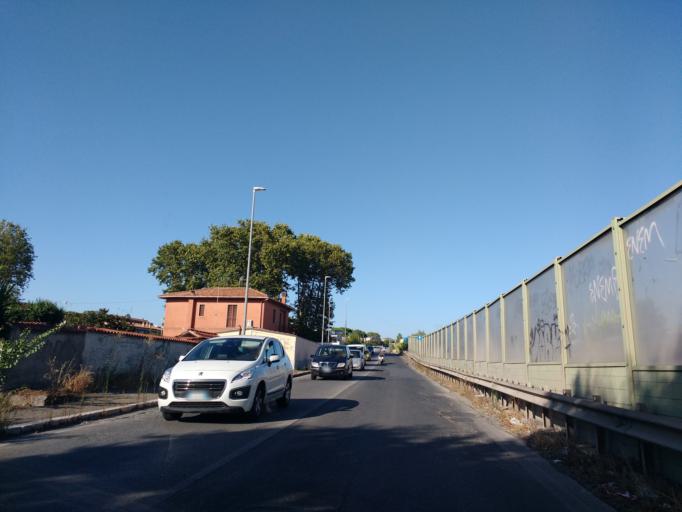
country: IT
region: Latium
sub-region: Citta metropolitana di Roma Capitale
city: Acilia-Castel Fusano-Ostia Antica
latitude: 41.7815
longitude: 12.3550
